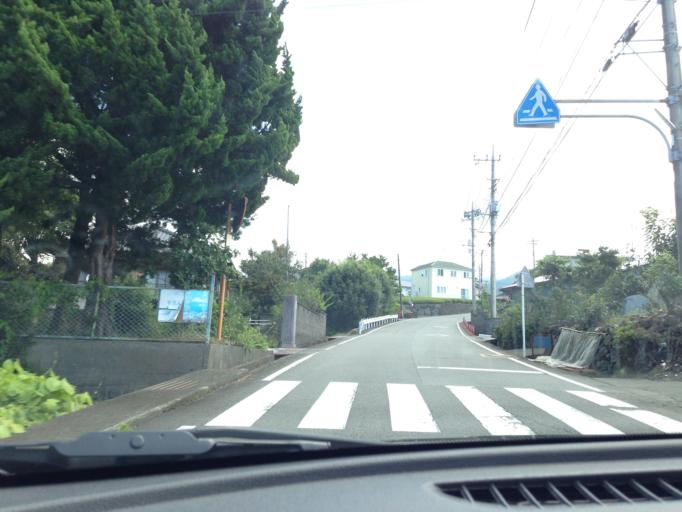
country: JP
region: Shizuoka
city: Fuji
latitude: 35.1982
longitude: 138.7173
